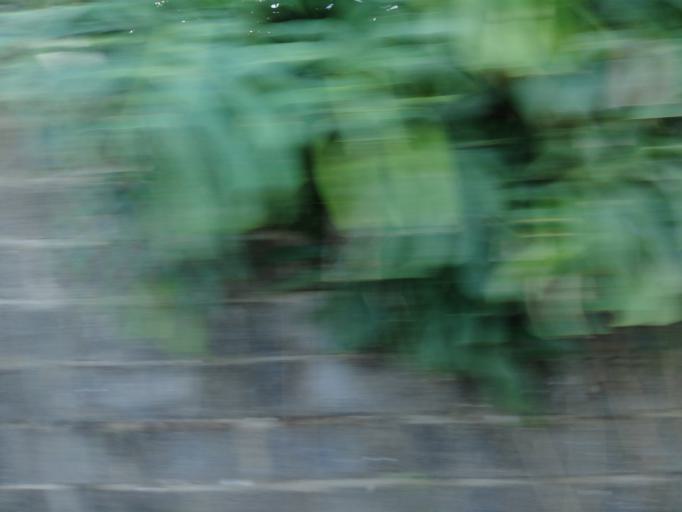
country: MU
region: Moka
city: Verdun
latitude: -20.2245
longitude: 57.5451
